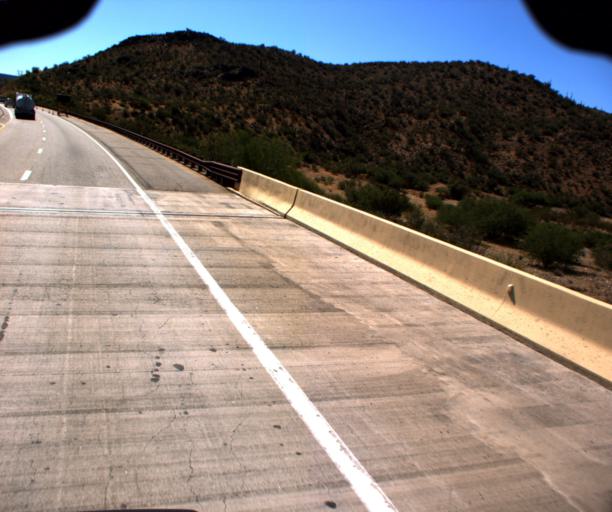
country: US
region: Arizona
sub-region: Yavapai County
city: Bagdad
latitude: 34.3686
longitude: -113.1845
